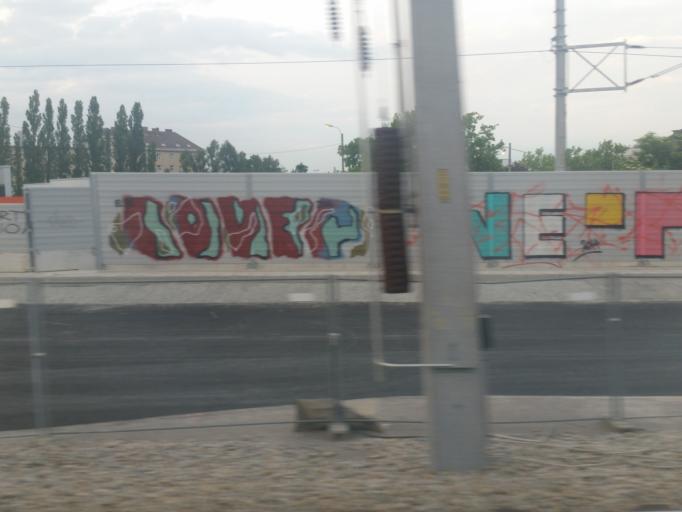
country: AT
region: Vienna
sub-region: Wien Stadt
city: Vienna
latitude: 48.1752
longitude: 16.3955
